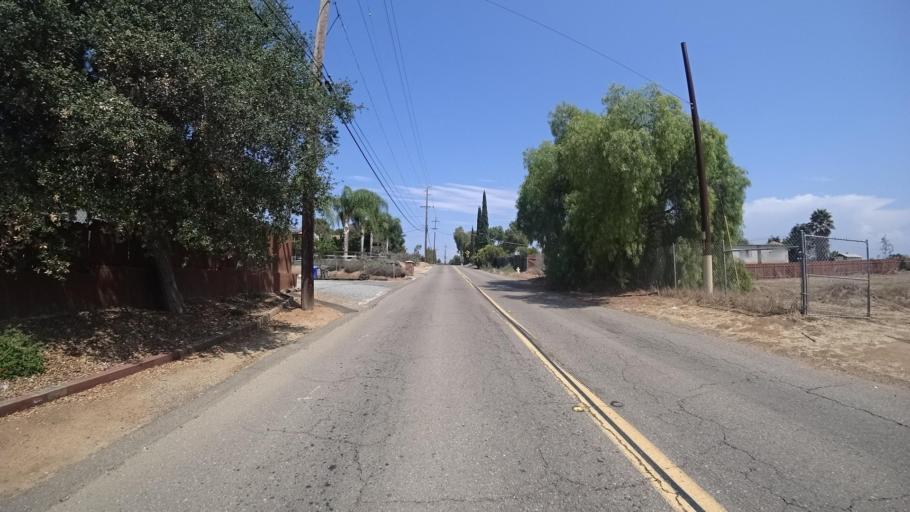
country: US
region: California
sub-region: San Diego County
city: Fallbrook
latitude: 33.3605
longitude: -117.2319
